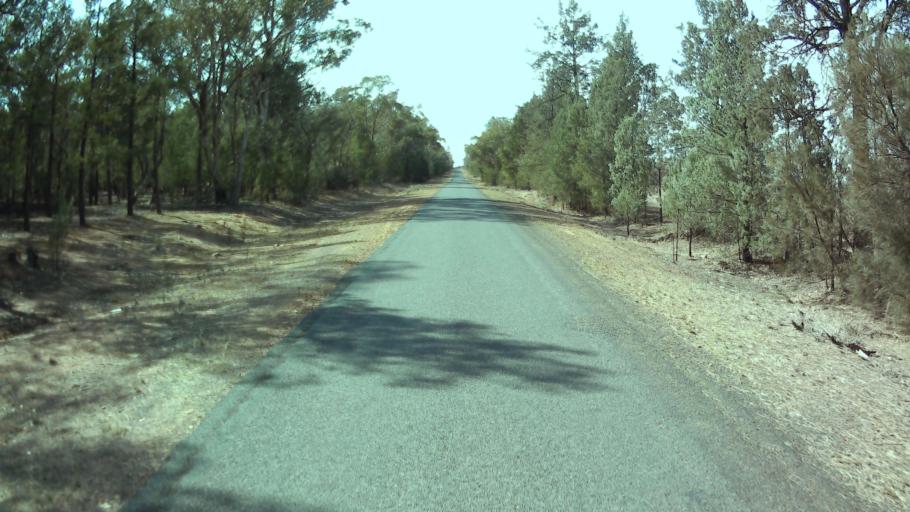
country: AU
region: New South Wales
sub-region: Weddin
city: Grenfell
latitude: -33.7274
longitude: 148.0332
